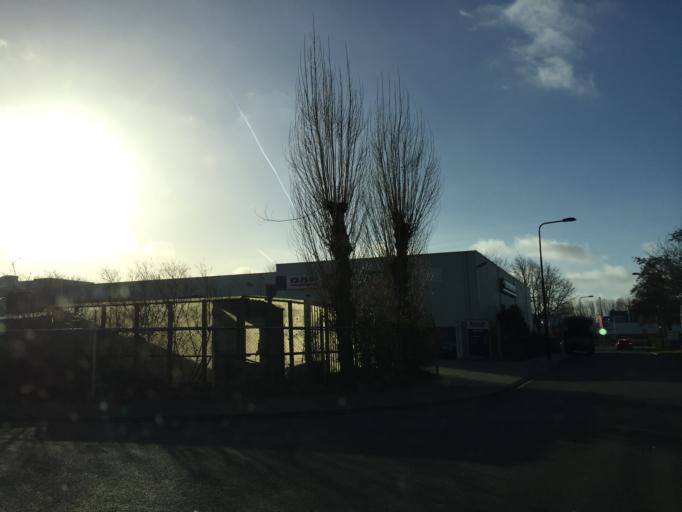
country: NL
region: South Holland
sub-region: Gemeente Gouda
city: Bloemendaal
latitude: 52.0245
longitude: 4.6804
